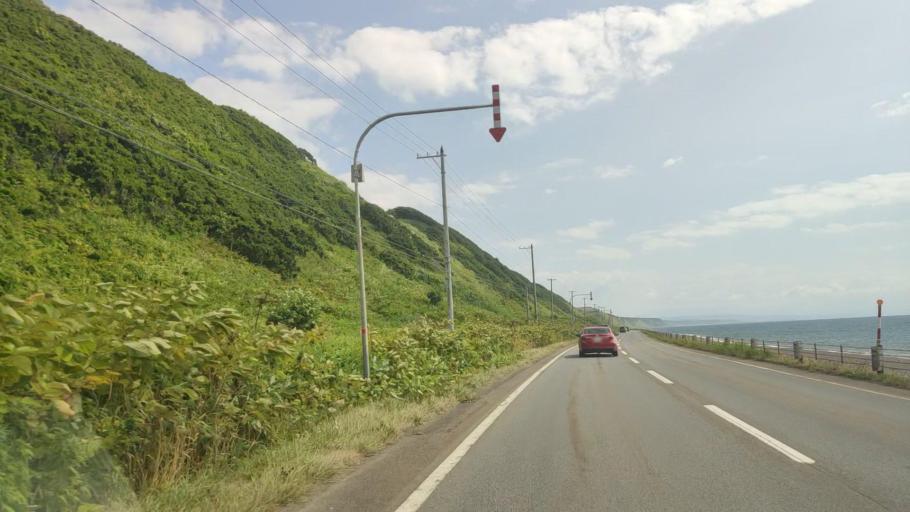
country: JP
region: Hokkaido
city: Rumoi
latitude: 44.0854
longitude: 141.6621
